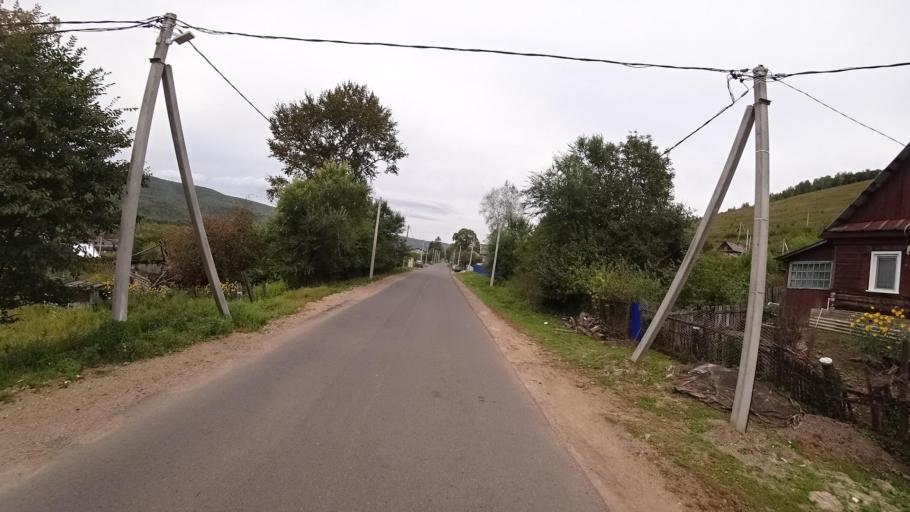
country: RU
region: Jewish Autonomous Oblast
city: Khingansk
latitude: 49.0236
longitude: 131.0595
